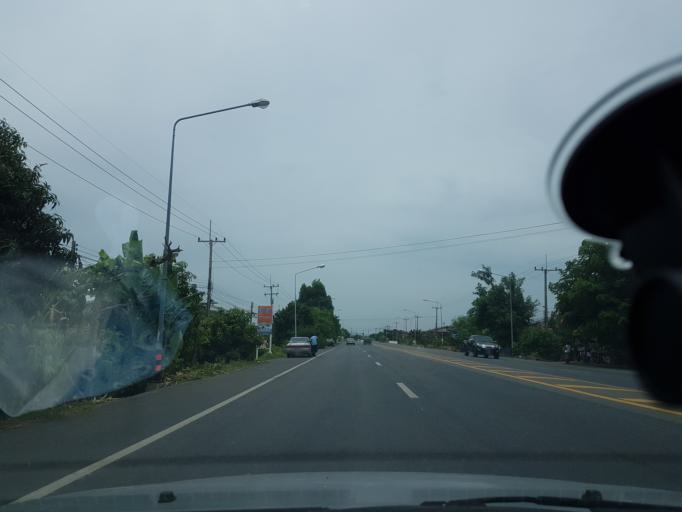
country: TH
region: Lop Buri
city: Lop Buri
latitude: 14.8091
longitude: 100.5868
